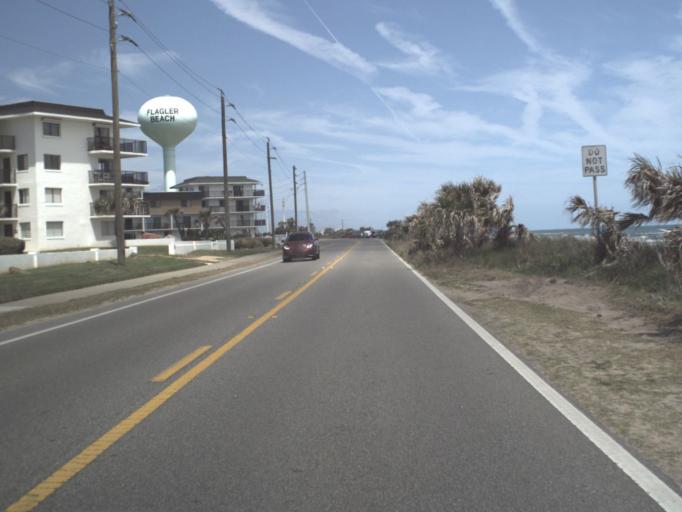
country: US
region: Florida
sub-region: Flagler County
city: Flagler Beach
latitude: 29.4328
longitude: -81.1051
